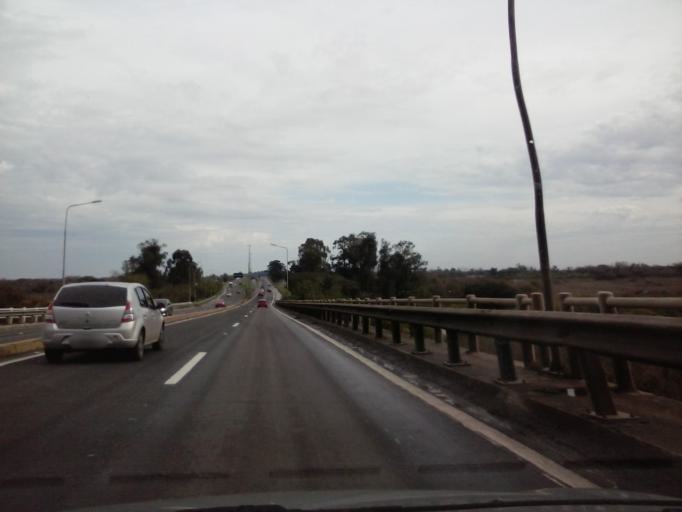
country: BR
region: Rio Grande do Sul
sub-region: Porto Alegre
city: Porto Alegre
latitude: -29.9963
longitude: -51.2120
